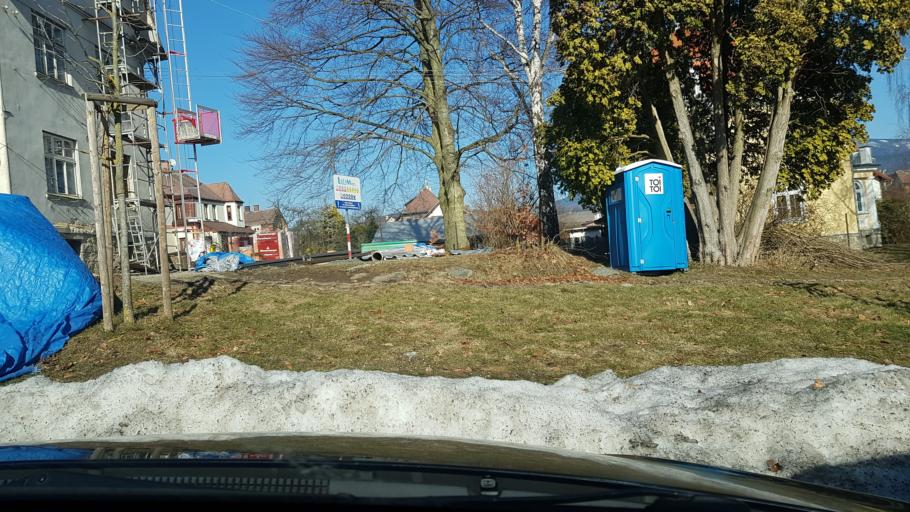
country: CZ
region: Olomoucky
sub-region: Okres Sumperk
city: Velke Losiny
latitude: 50.0356
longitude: 17.0402
